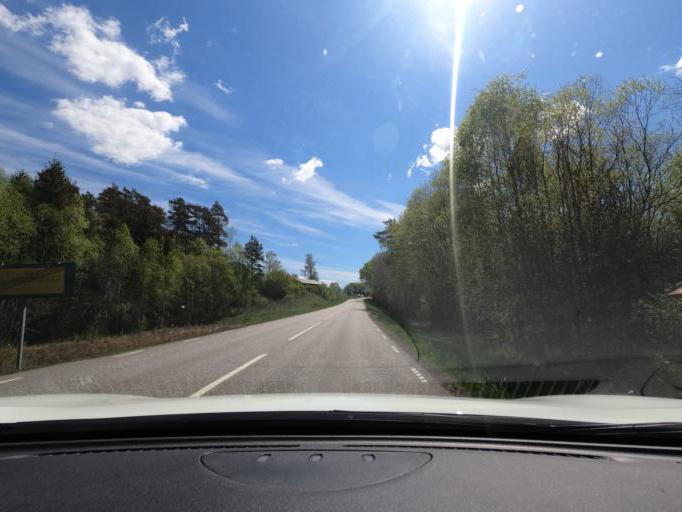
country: SE
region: Halland
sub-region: Kungsbacka Kommun
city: Fjaeras kyrkby
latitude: 57.3950
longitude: 12.2443
